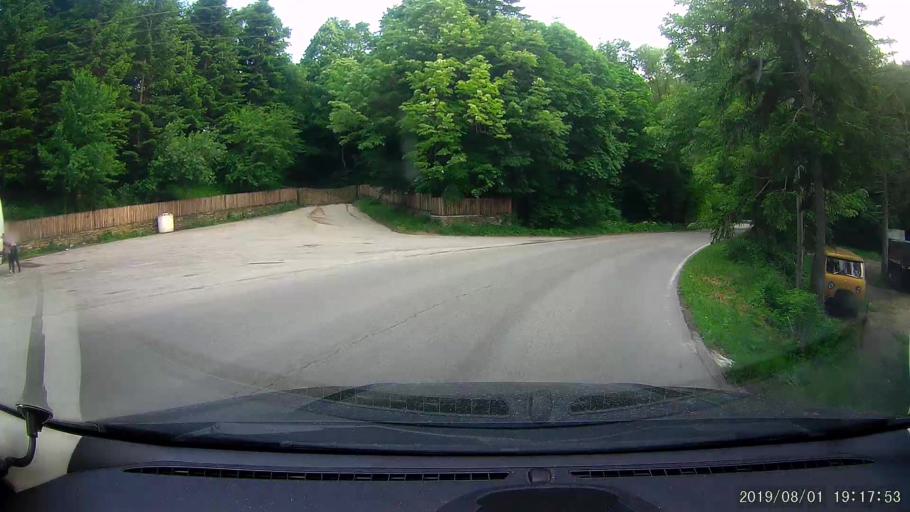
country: BG
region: Shumen
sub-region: Obshtina Smyadovo
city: Smyadovo
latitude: 42.9186
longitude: 26.9393
